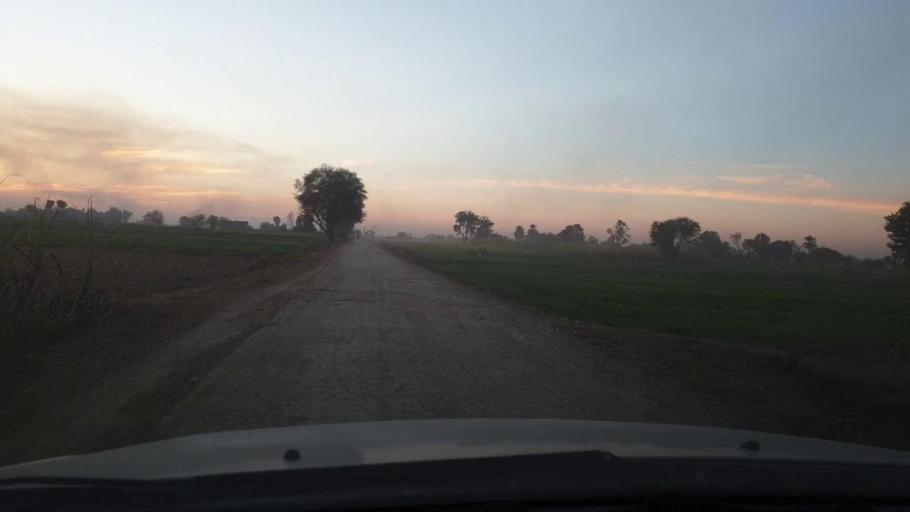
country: PK
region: Sindh
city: Ghotki
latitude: 27.9827
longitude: 69.2770
